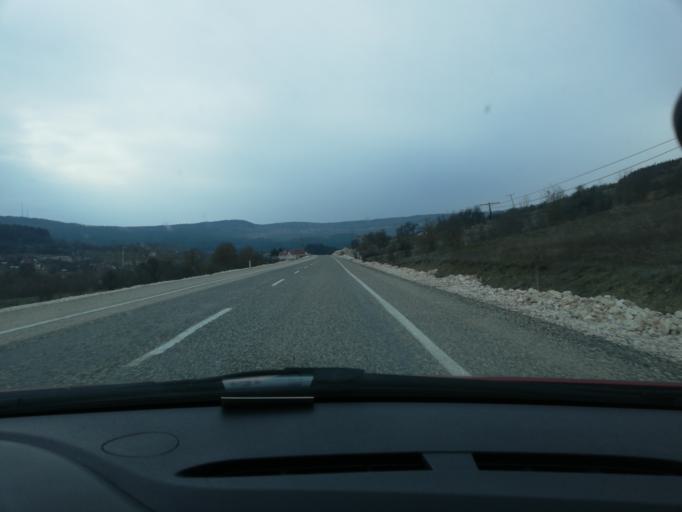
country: TR
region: Kastamonu
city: Pinarbasi
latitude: 41.5930
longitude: 33.0968
